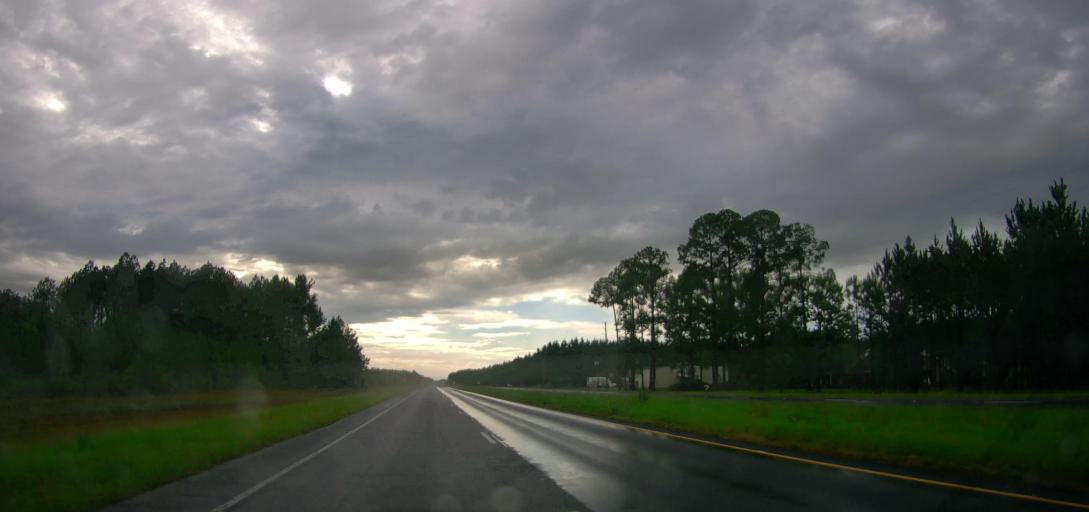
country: US
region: Georgia
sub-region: Ware County
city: Deenwood
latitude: 31.2572
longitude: -82.4949
